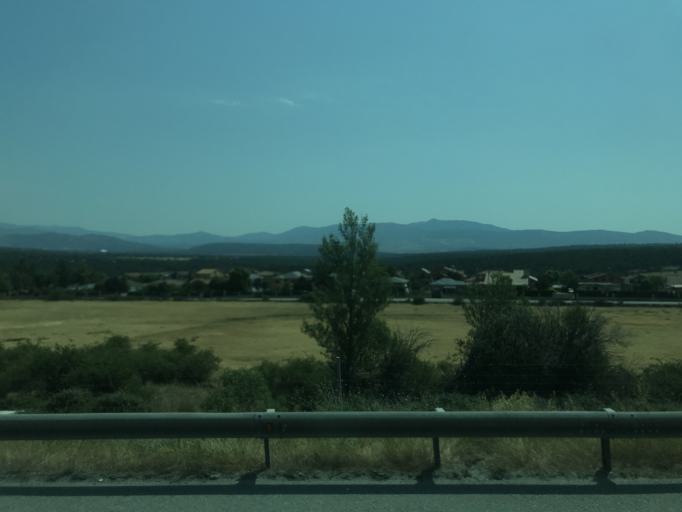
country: ES
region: Madrid
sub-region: Provincia de Madrid
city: Buitrago del Lozoya
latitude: 40.9843
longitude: -3.6397
